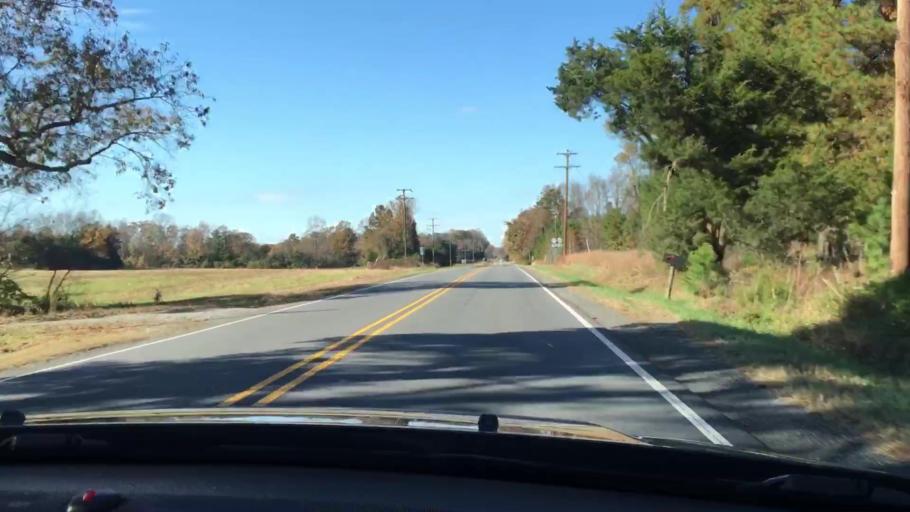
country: US
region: Virginia
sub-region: King William County
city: King William
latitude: 37.7024
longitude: -77.0453
